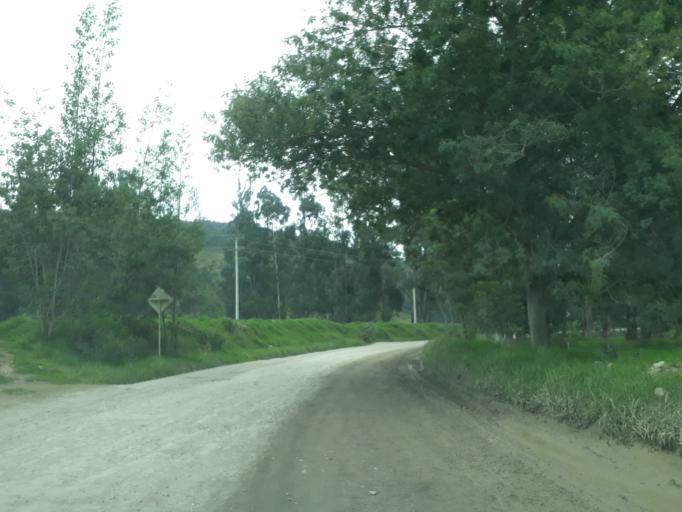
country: CO
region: Cundinamarca
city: Lenguazaque
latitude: 5.3260
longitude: -73.7548
